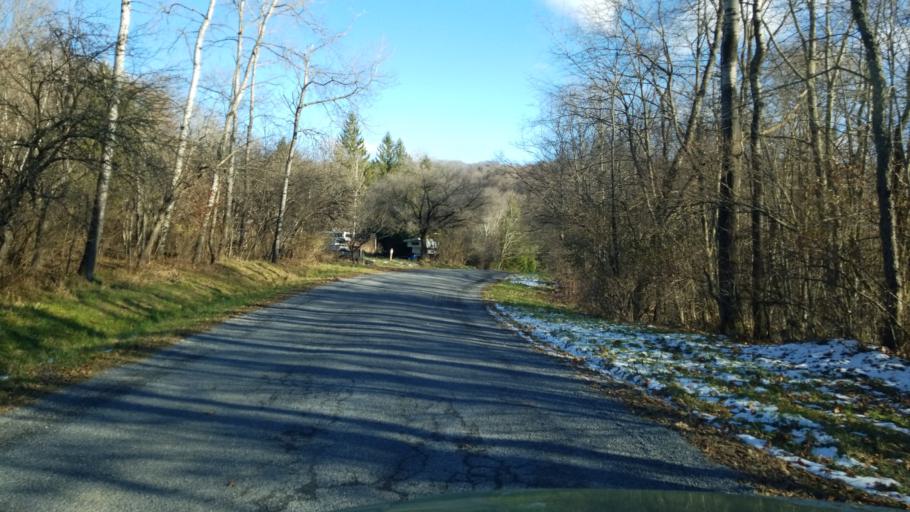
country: US
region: Pennsylvania
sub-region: Jefferson County
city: Brockway
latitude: 41.2596
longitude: -78.8007
